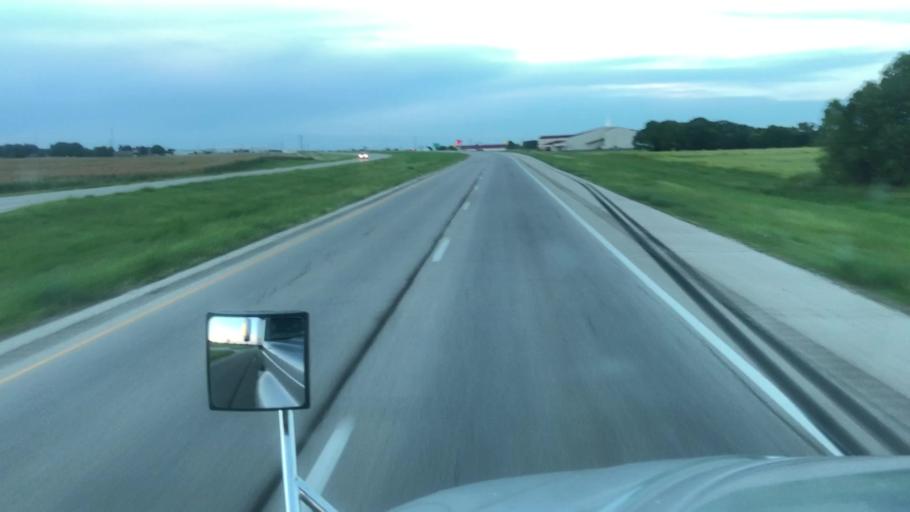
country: US
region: Oklahoma
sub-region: Kay County
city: Ponca City
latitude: 36.7613
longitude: -97.0635
